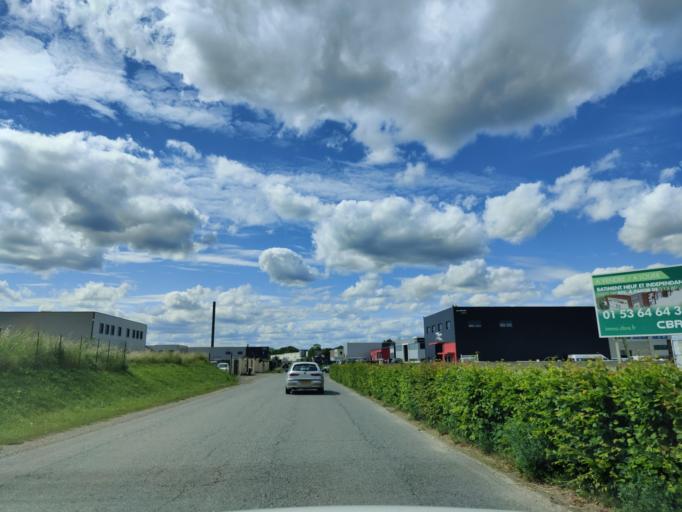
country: FR
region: Ile-de-France
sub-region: Departement de l'Essonne
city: Egly
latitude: 48.5722
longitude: 2.2084
